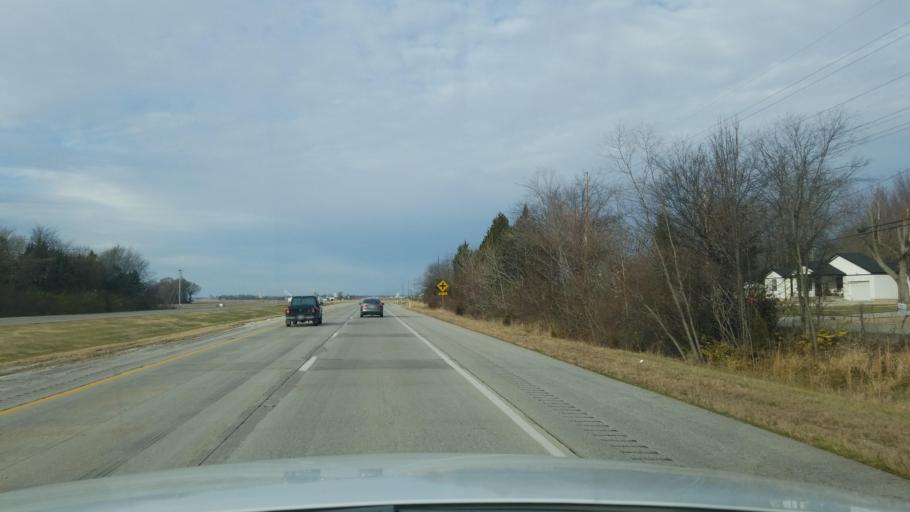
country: US
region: Indiana
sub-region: Posey County
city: Mount Vernon
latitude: 37.9421
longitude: -87.7517
